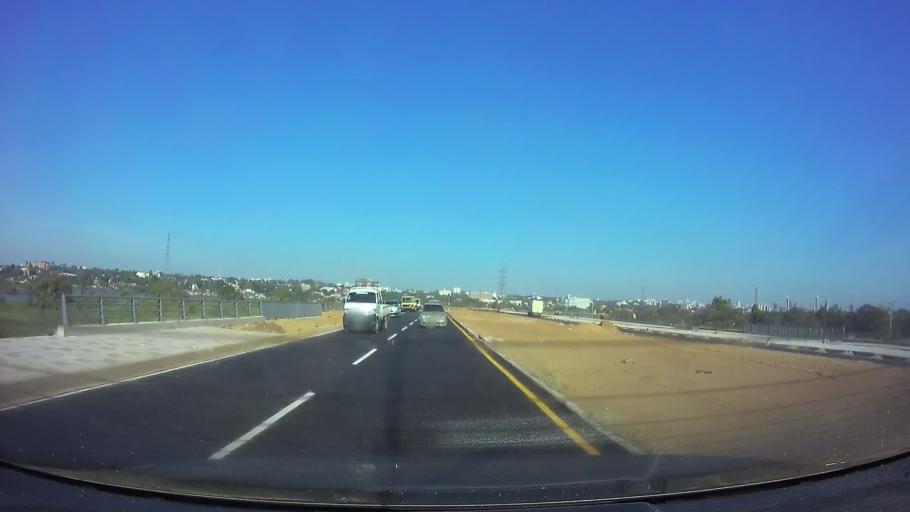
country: PY
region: Asuncion
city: Asuncion
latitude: -25.2590
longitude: -57.6076
